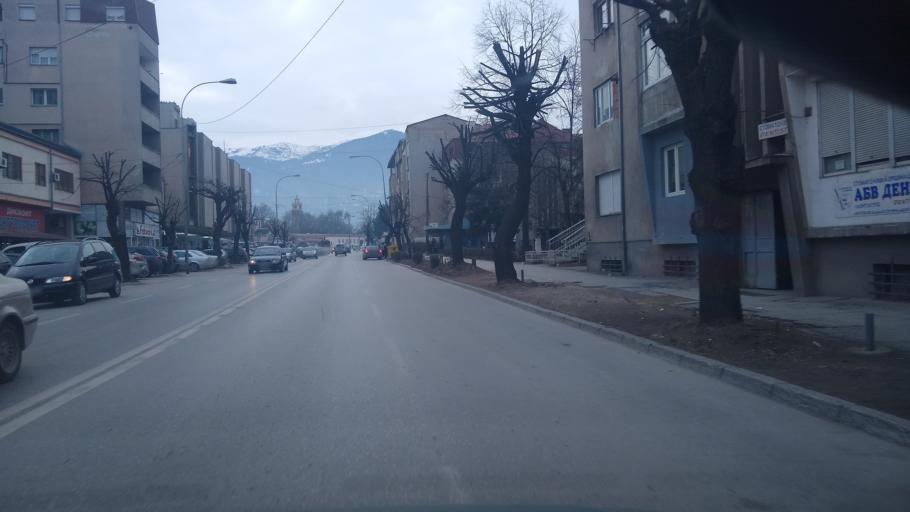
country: MK
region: Bitola
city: Bitola
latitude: 41.0337
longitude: 21.3379
